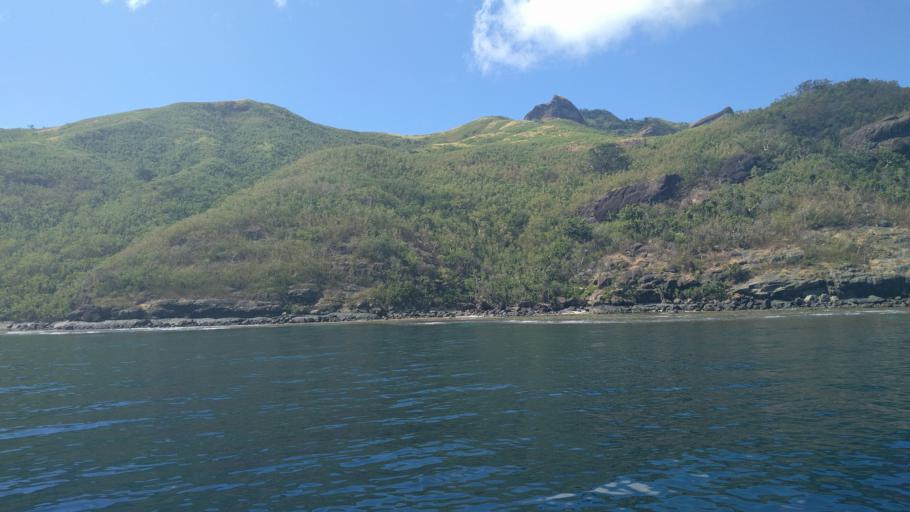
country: FJ
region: Western
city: Lautoka
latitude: -17.2860
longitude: 177.1018
